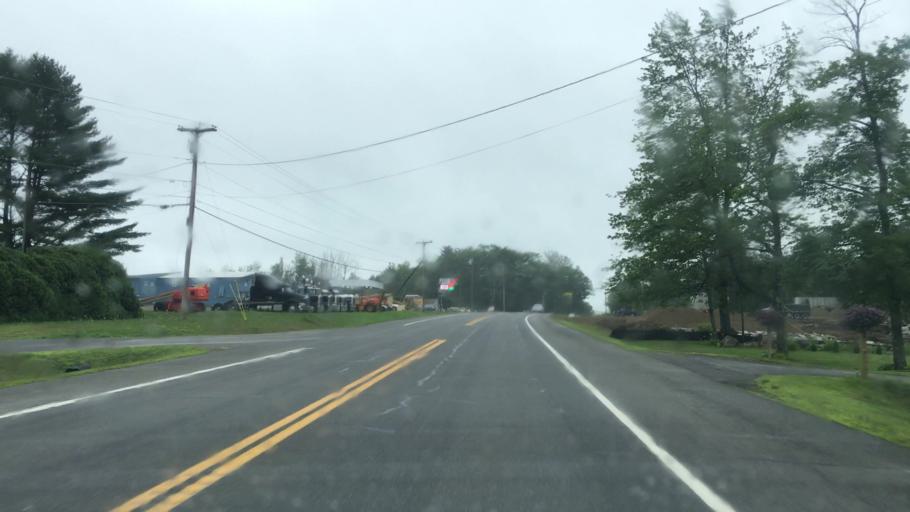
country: US
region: Maine
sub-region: Kennebec County
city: Windsor
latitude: 44.2536
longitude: -69.5444
